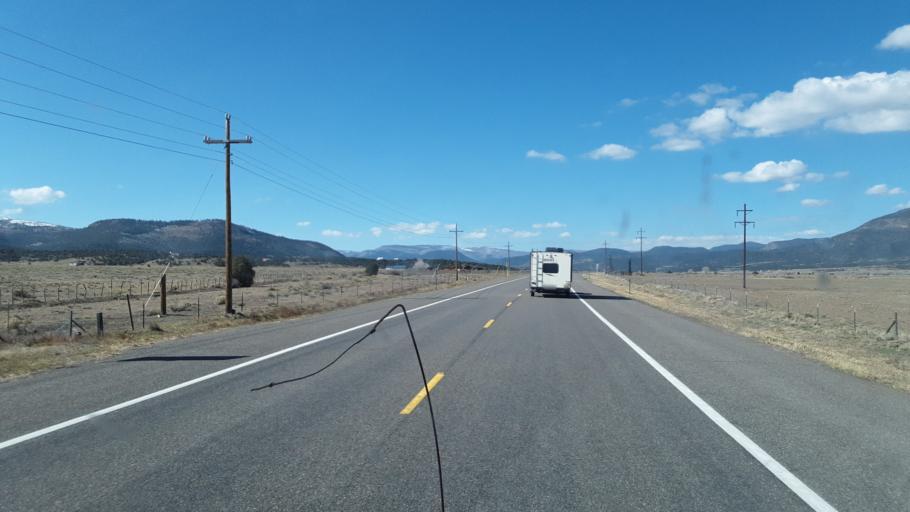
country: US
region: Colorado
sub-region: Rio Grande County
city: Del Norte
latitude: 37.6774
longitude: -106.4966
